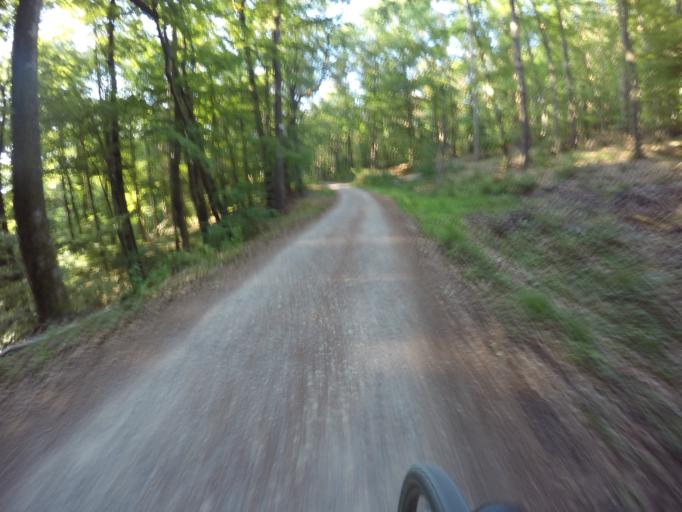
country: DE
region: Baden-Wuerttemberg
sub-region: Regierungsbezirk Stuttgart
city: Esslingen
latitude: 48.7738
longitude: 9.3144
